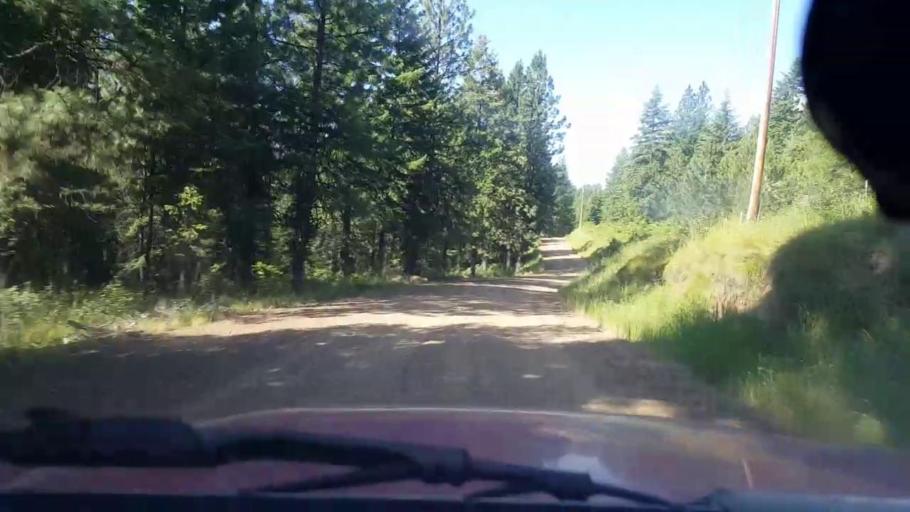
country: US
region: Washington
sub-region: Garfield County
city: Pomeroy
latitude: 46.0364
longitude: -117.4461
